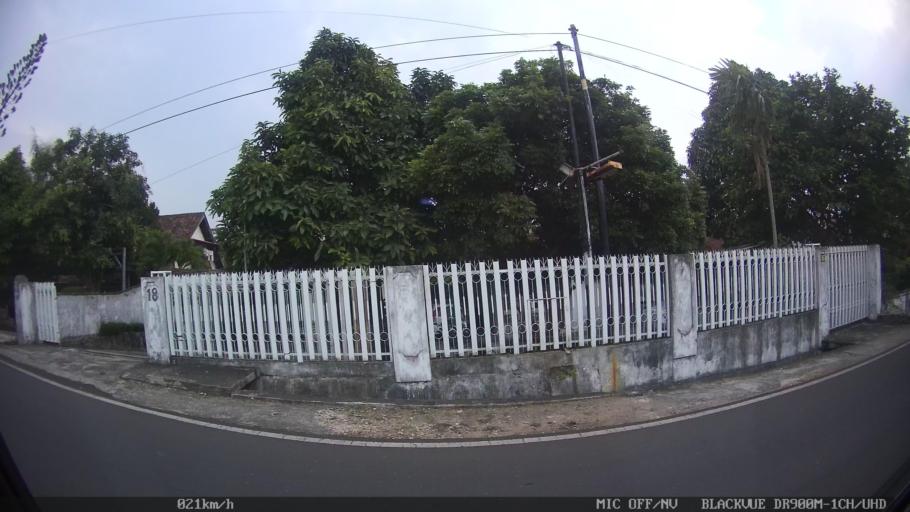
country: ID
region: Lampung
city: Bandarlampung
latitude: -5.4250
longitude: 105.2573
